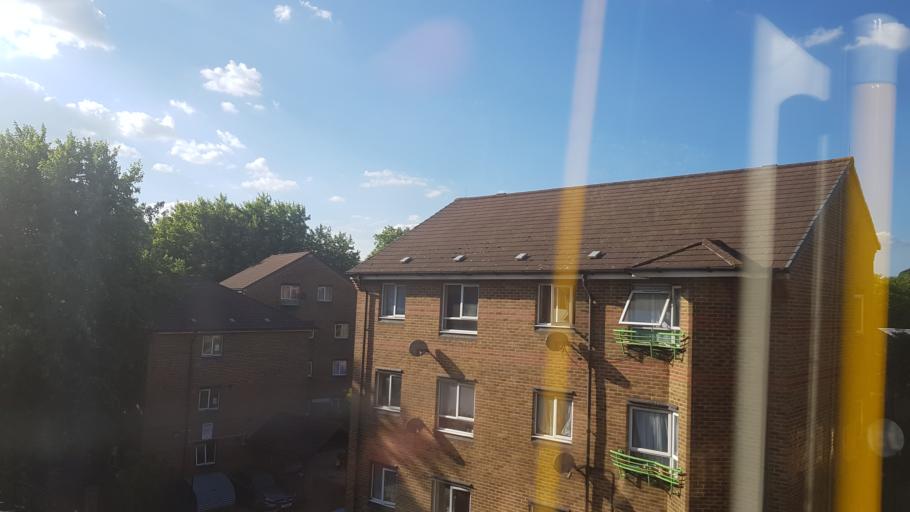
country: GB
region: England
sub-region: Greater London
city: Hammersmith
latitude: 51.5153
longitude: -0.2156
